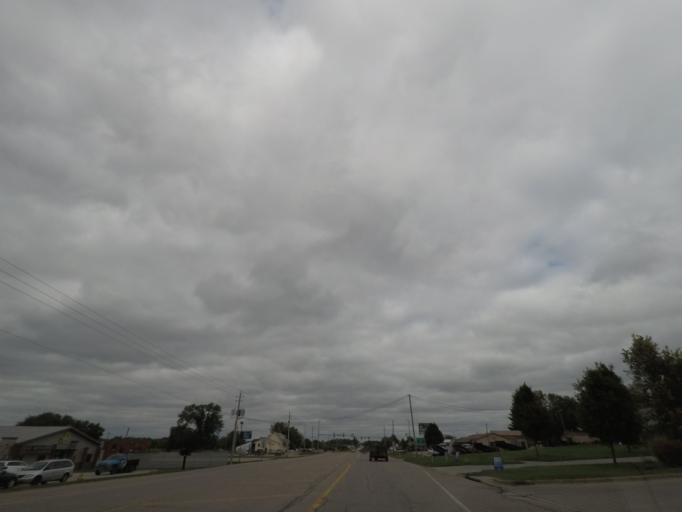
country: US
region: Iowa
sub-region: Polk County
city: Saylorville
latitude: 41.6788
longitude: -93.6006
